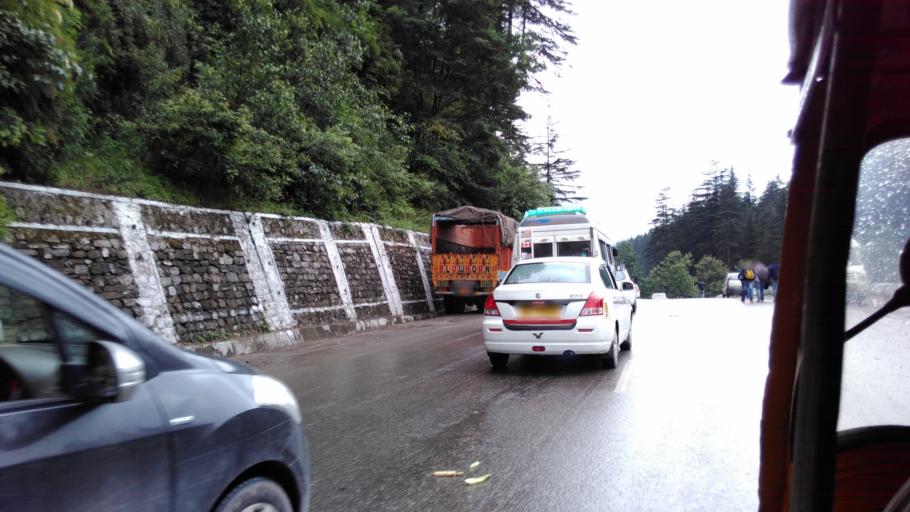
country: IN
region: Himachal Pradesh
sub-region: Kulu
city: Manali
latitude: 32.2551
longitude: 77.1888
